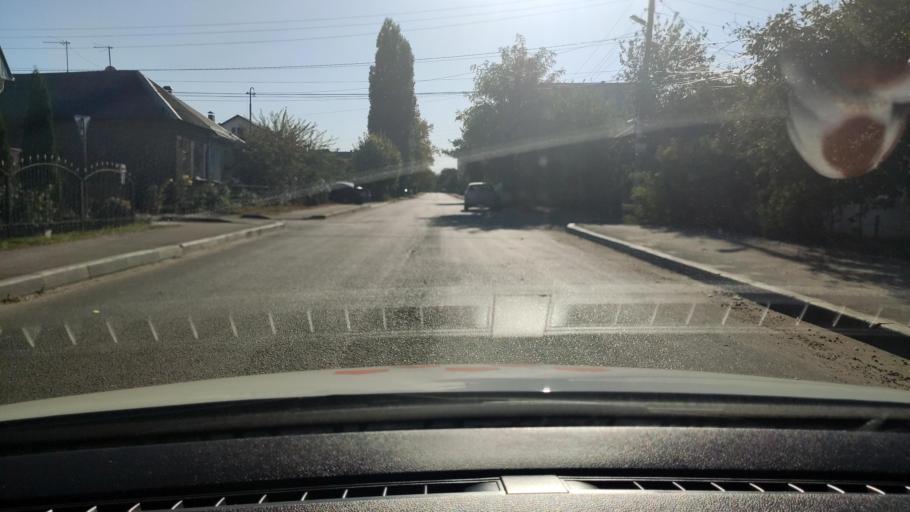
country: RU
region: Voronezj
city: Voronezh
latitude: 51.6834
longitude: 39.1426
